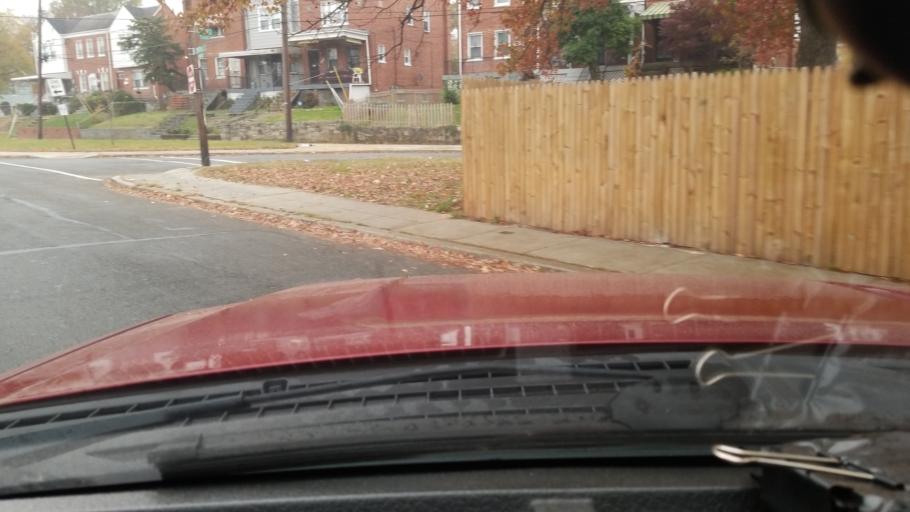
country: US
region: Maryland
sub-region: Prince George's County
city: Capitol Heights
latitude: 38.8868
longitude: -76.9244
